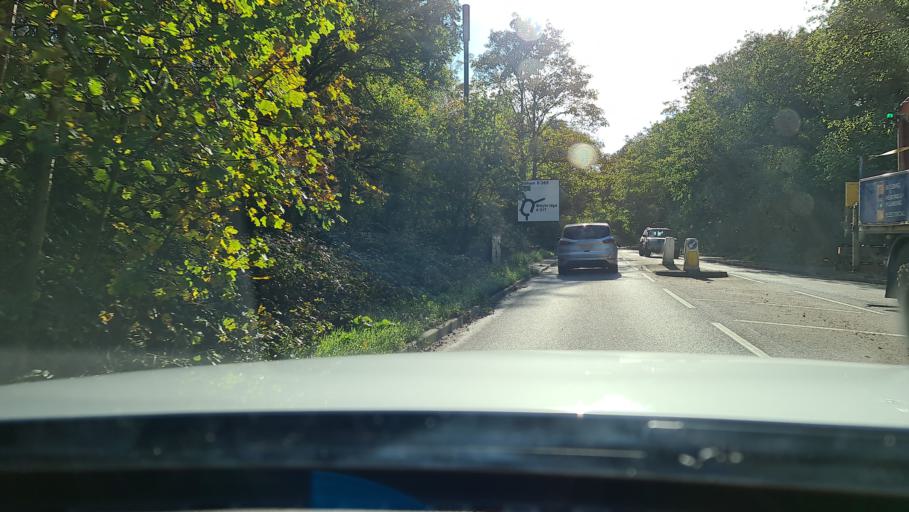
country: GB
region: England
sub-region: Surrey
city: Walton-on-Thames
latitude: 51.3676
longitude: -0.4289
